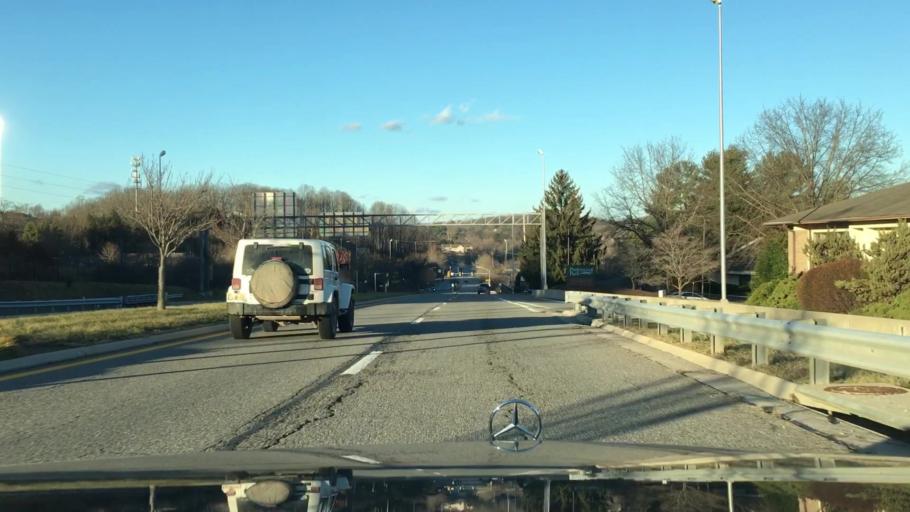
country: US
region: Virginia
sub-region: Montgomery County
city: Merrimac
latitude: 37.1956
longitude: -80.4021
